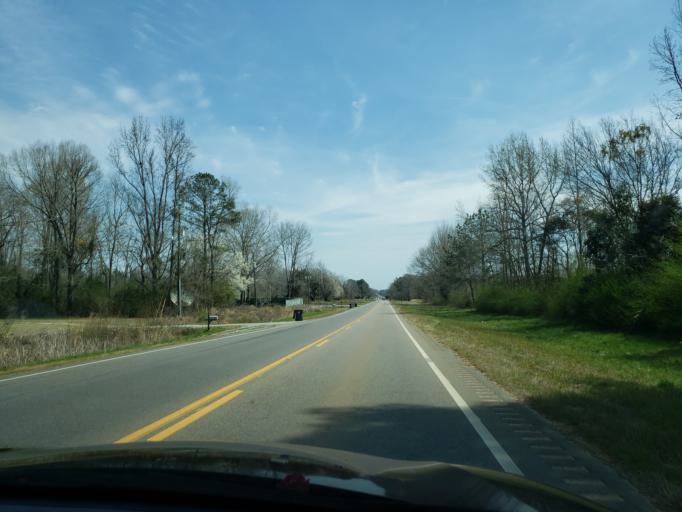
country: US
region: Alabama
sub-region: Autauga County
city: Prattville
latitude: 32.4306
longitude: -86.5252
